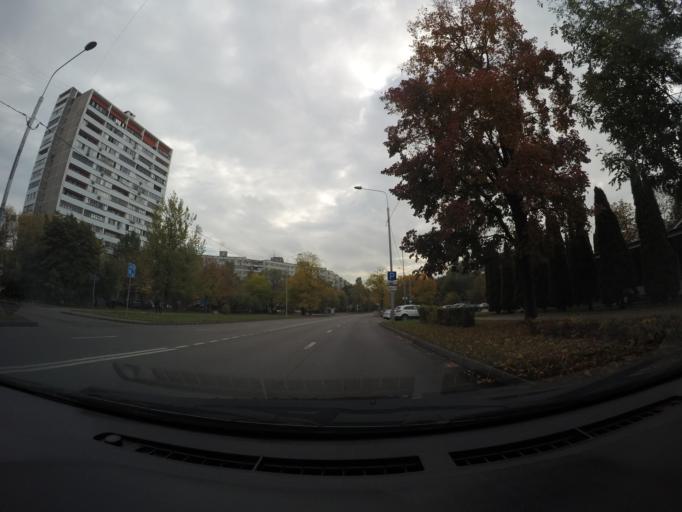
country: RU
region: Moscow
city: Ivanovskoye
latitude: 55.7661
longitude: 37.8224
